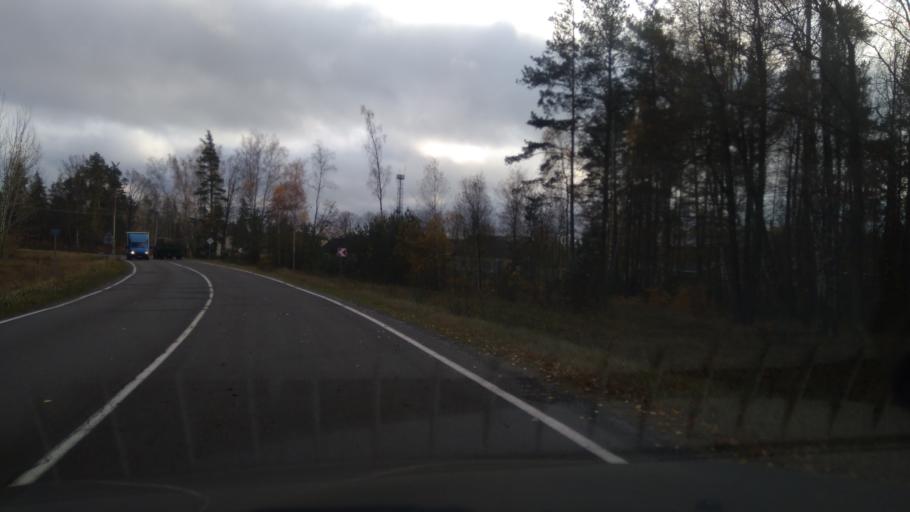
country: BY
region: Minsk
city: Slutsk
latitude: 53.2076
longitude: 27.7657
